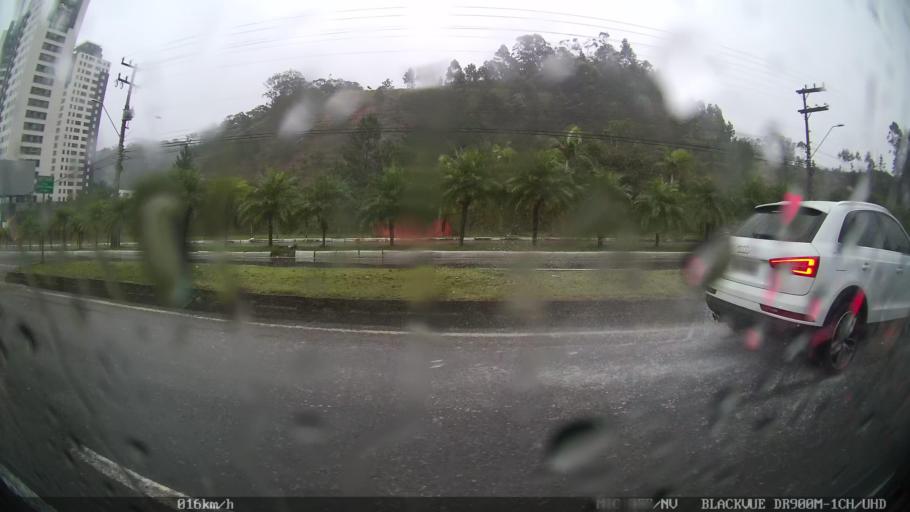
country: BR
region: Santa Catarina
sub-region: Itajai
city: Itajai
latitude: -26.9391
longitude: -48.6408
